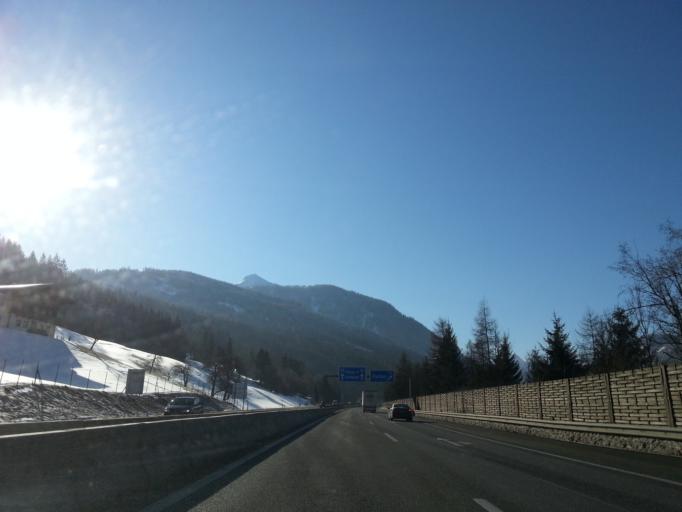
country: AT
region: Salzburg
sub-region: Politischer Bezirk Sankt Johann im Pongau
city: Flachau
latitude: 47.3654
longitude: 13.3959
